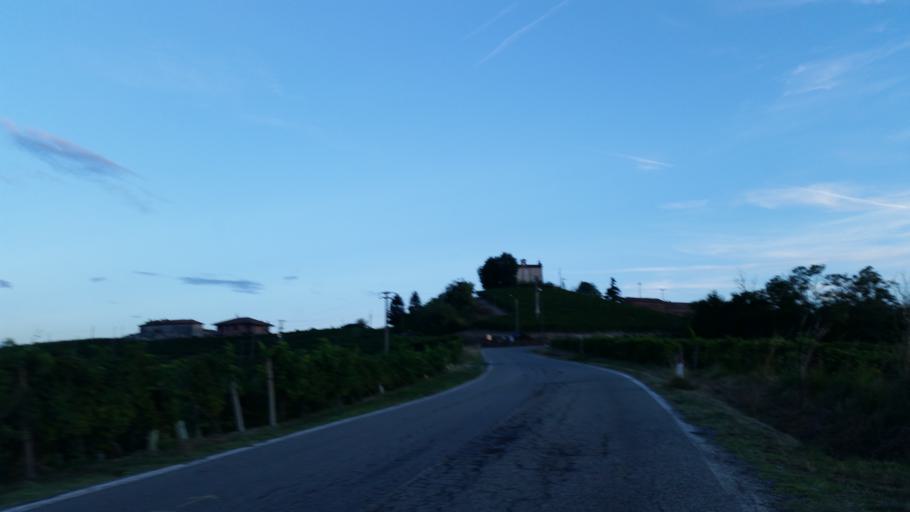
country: IT
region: Piedmont
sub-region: Provincia di Cuneo
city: Castiglione Tinella
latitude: 44.7205
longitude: 8.1875
